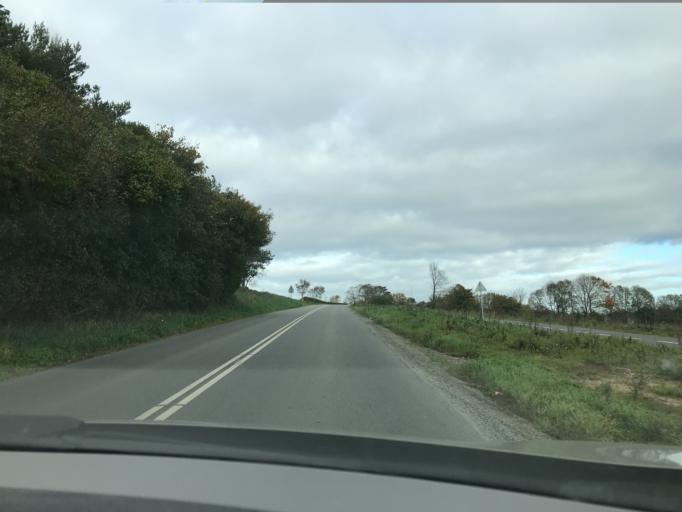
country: DK
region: South Denmark
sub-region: Kolding Kommune
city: Kolding
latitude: 55.5409
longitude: 9.4168
